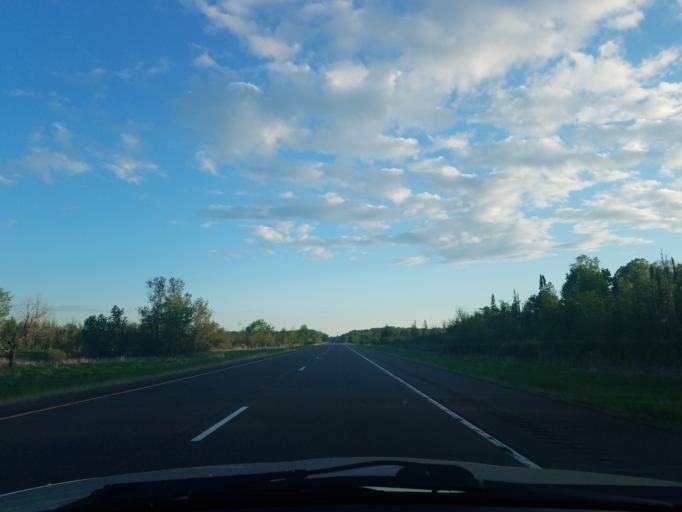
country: US
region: Minnesota
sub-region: Carlton County
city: Carlton
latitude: 46.6038
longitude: -92.5637
